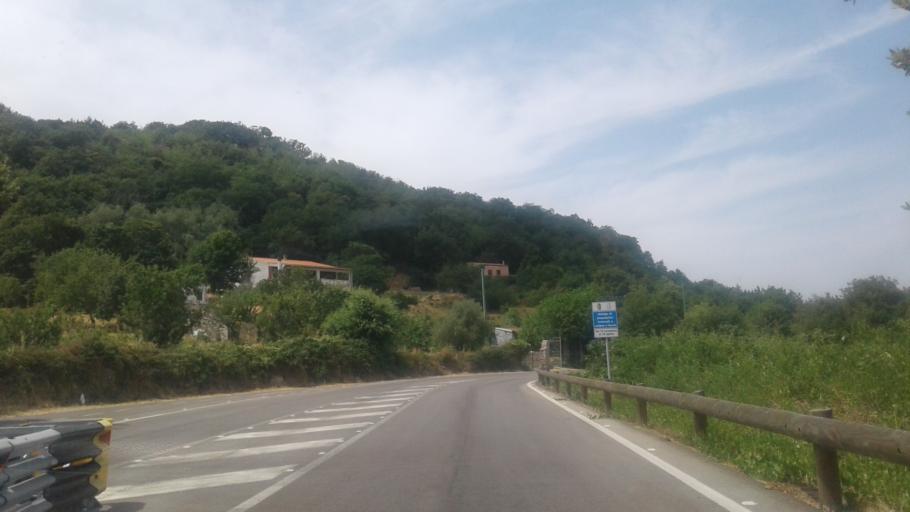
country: IT
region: Sardinia
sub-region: Provincia di Olbia-Tempio
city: Tempio Pausania
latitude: 40.9080
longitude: 9.0839
